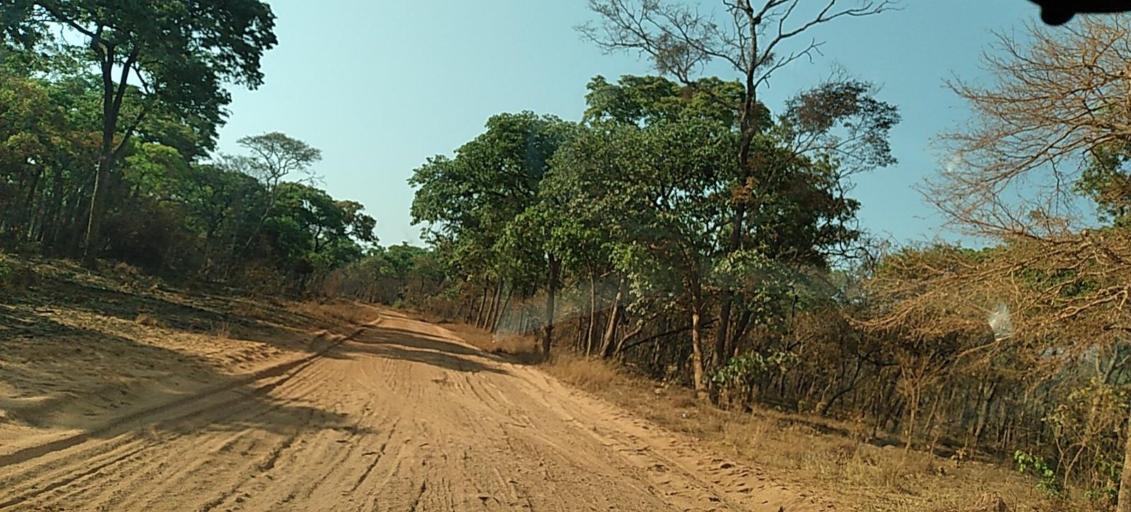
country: ZM
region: North-Western
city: Kasempa
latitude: -13.6642
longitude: 26.0112
